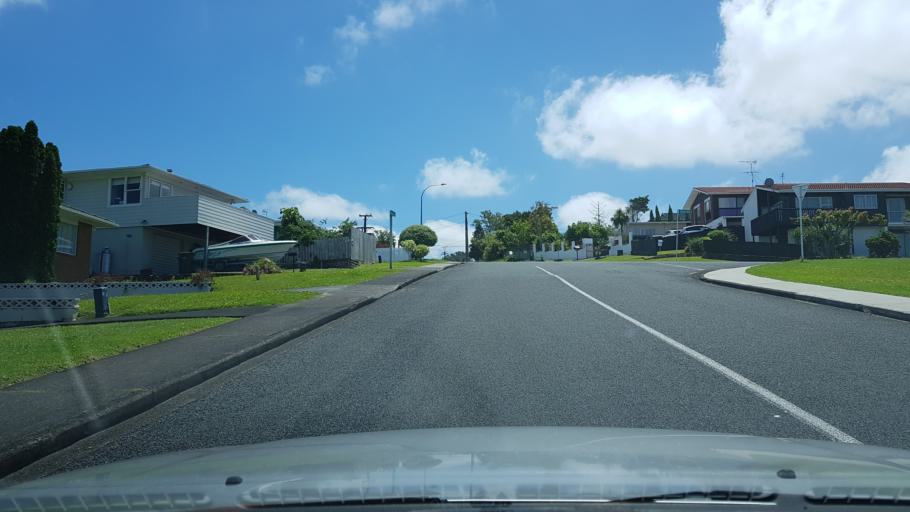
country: NZ
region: Auckland
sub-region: Auckland
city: North Shore
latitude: -36.7967
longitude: 174.7306
